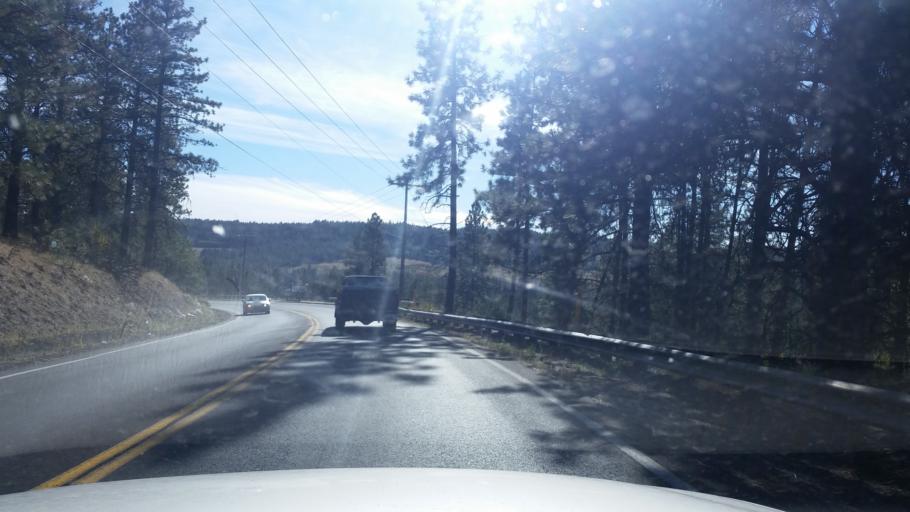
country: US
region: Washington
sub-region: Spokane County
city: Spokane
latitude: 47.5968
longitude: -117.3920
